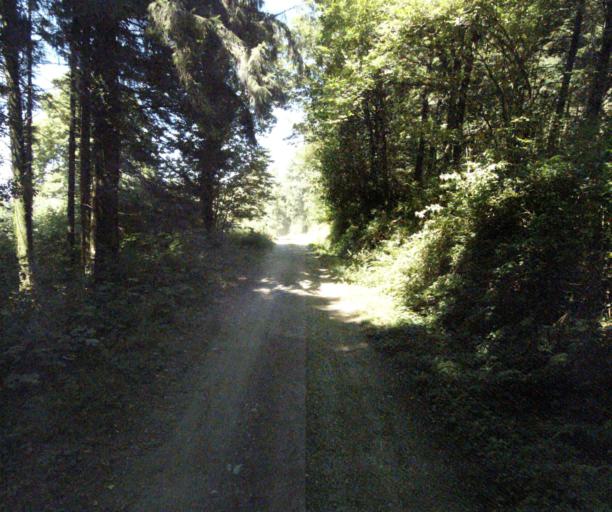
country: FR
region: Midi-Pyrenees
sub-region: Departement du Tarn
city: Soreze
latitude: 43.4421
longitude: 2.1072
